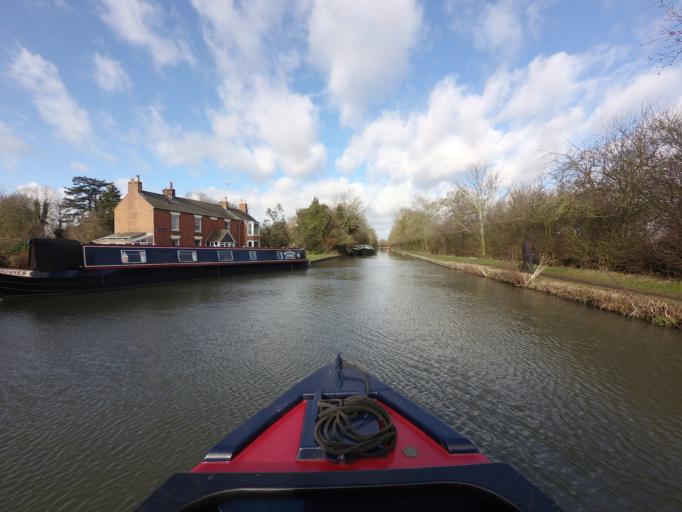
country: GB
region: England
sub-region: Northamptonshire
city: Bugbrooke
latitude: 52.2260
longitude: -1.0722
